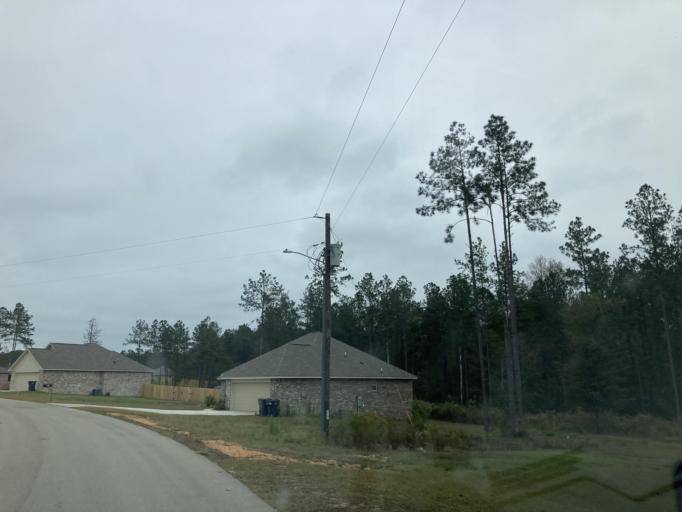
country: US
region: Mississippi
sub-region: Lamar County
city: Purvis
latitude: 31.1781
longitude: -89.4240
